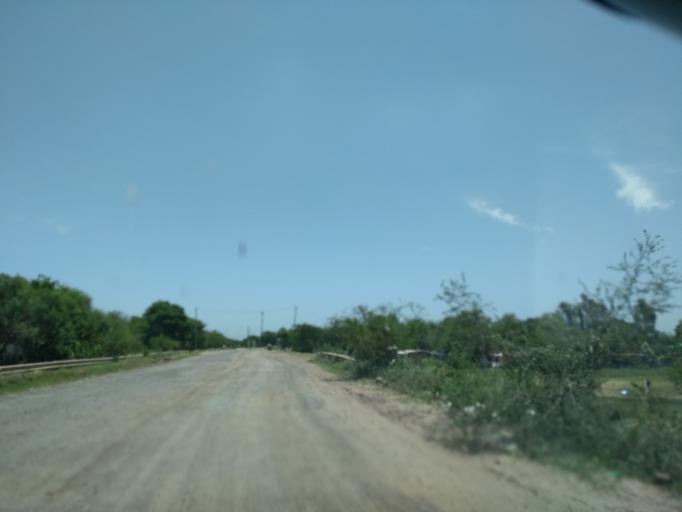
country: AR
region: Chaco
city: Barranqueras
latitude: -27.4658
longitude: -58.9124
